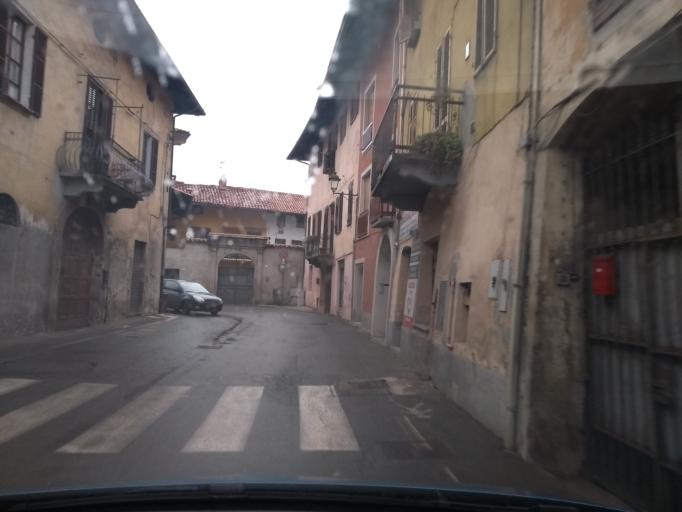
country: IT
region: Piedmont
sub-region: Provincia di Torino
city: Valperga
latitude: 45.3712
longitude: 7.6574
